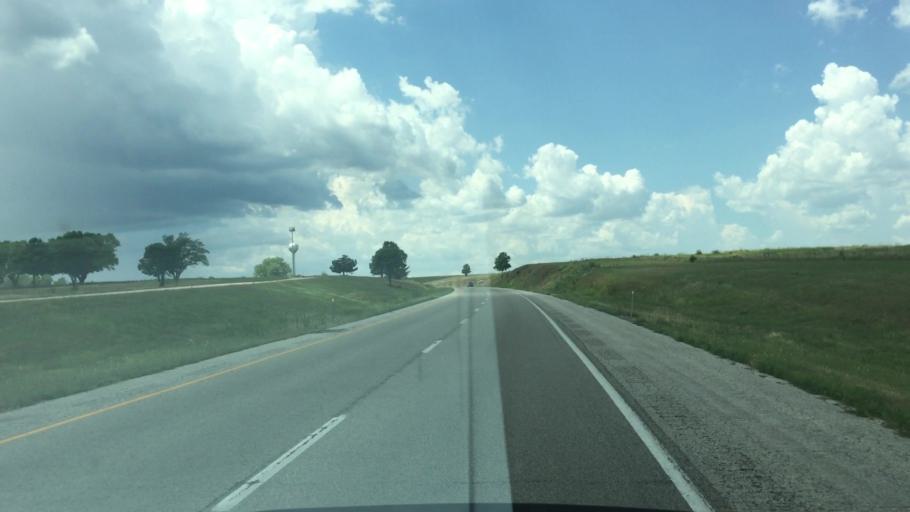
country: US
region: Kansas
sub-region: Shawnee County
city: Topeka
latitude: 39.0316
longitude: -95.5992
